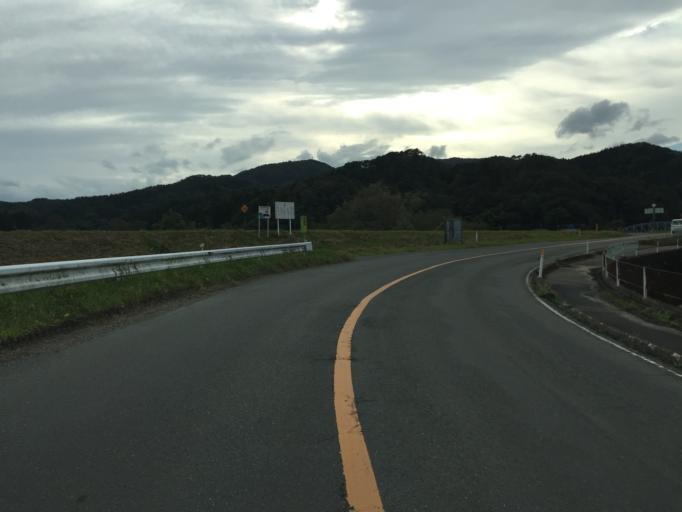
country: JP
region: Miyagi
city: Marumori
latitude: 37.9215
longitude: 140.7669
